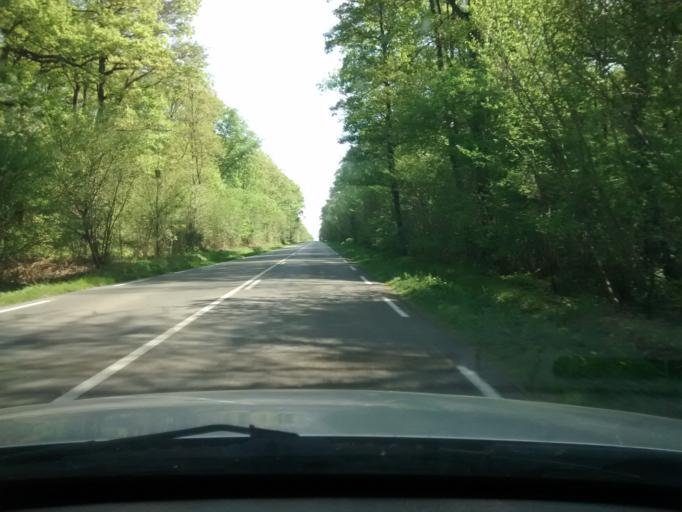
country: FR
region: Pays de la Loire
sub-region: Departement de la Mayenne
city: Montsurs
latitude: 48.1051
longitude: -0.5027
